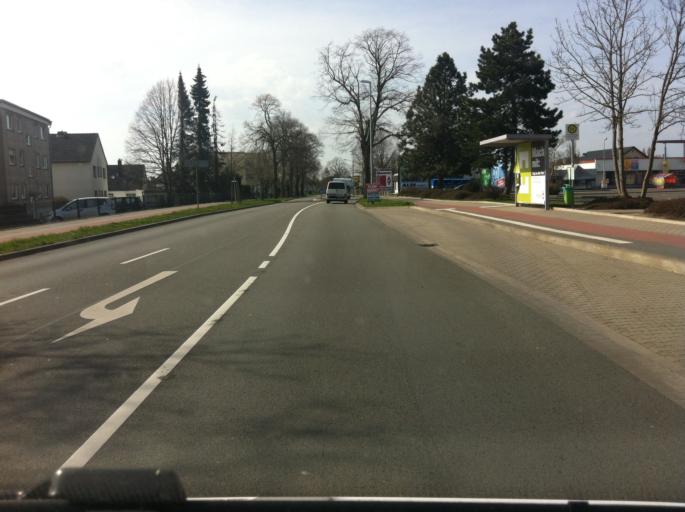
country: DE
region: North Rhine-Westphalia
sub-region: Regierungsbezirk Detmold
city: Minden
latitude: 52.2910
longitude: 8.8867
